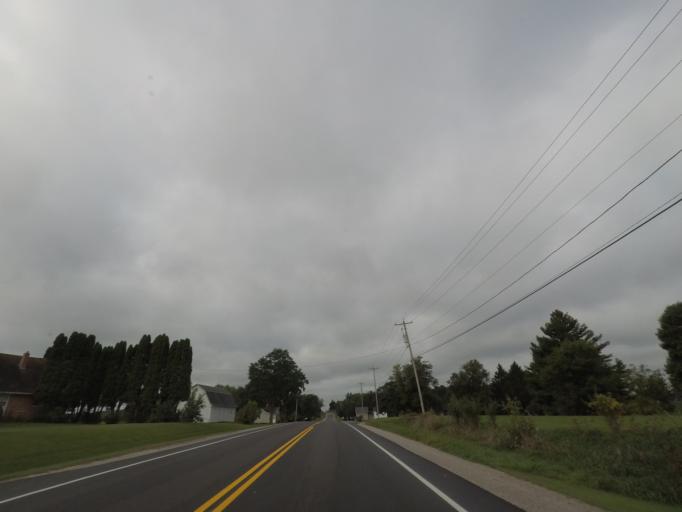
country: US
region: Wisconsin
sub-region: Jefferson County
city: Jefferson
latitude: 43.0083
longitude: -88.7719
